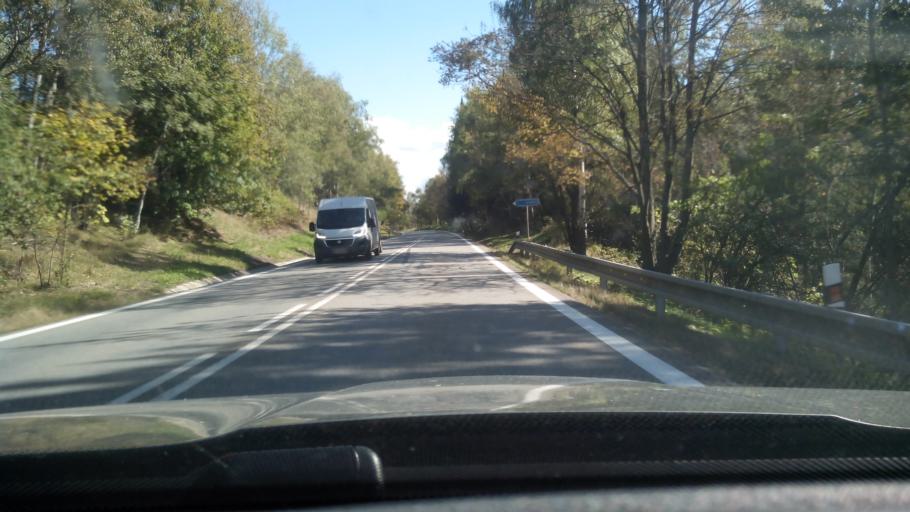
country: CZ
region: Jihocesky
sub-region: Okres Prachatice
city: Vimperk
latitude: 49.0620
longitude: 13.7553
